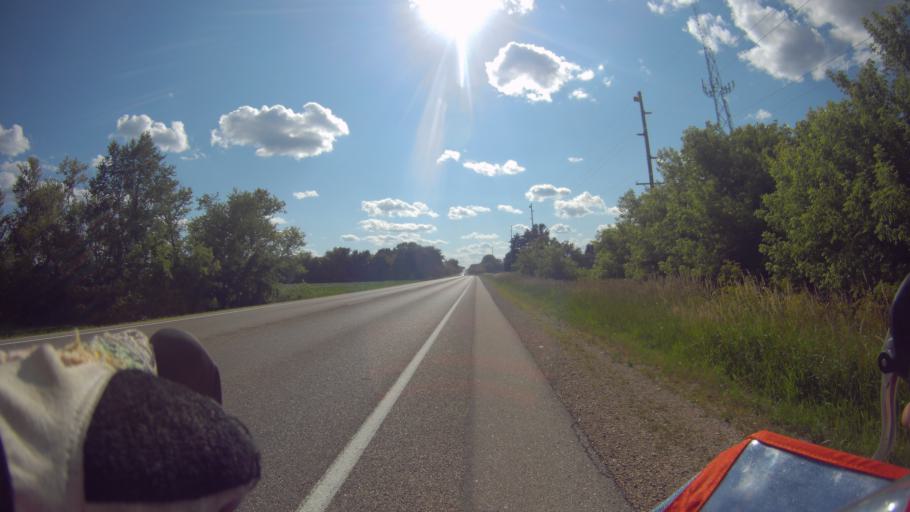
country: US
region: Wisconsin
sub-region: Dane County
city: Oregon
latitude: 42.9189
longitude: -89.3082
